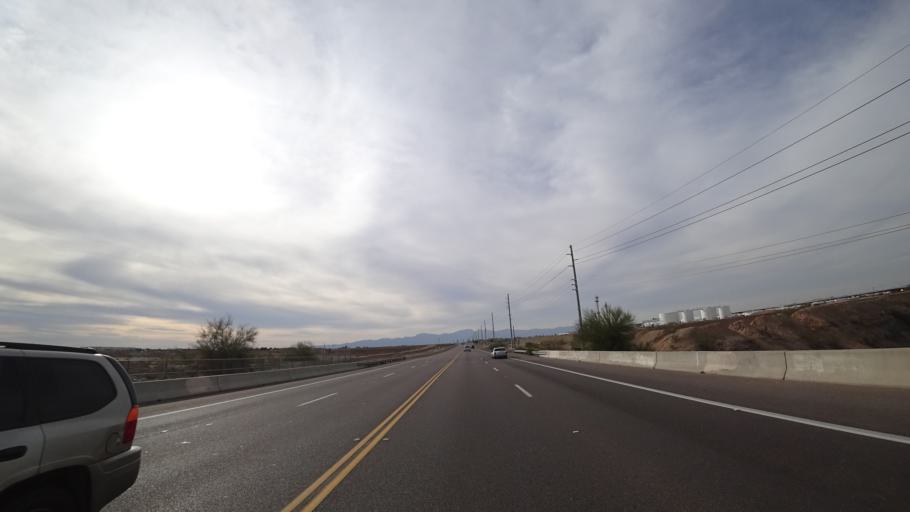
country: US
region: Arizona
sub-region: Maricopa County
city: Youngtown
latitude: 33.5654
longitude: -112.3177
